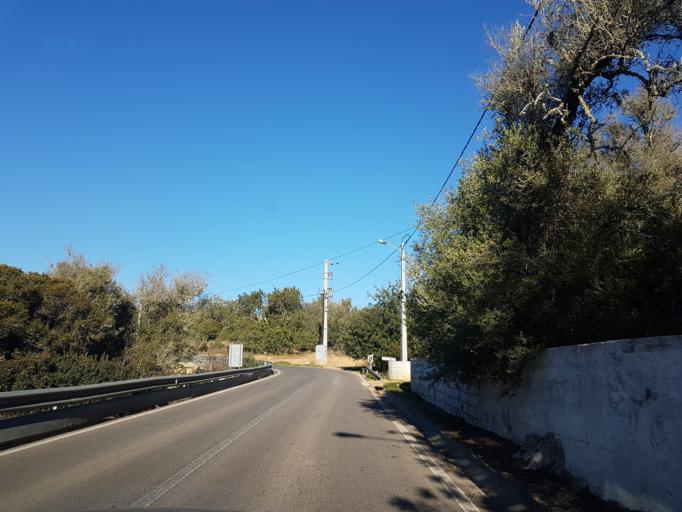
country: PT
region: Faro
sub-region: Lagoa
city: Lagoa
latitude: 37.1162
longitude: -8.4100
